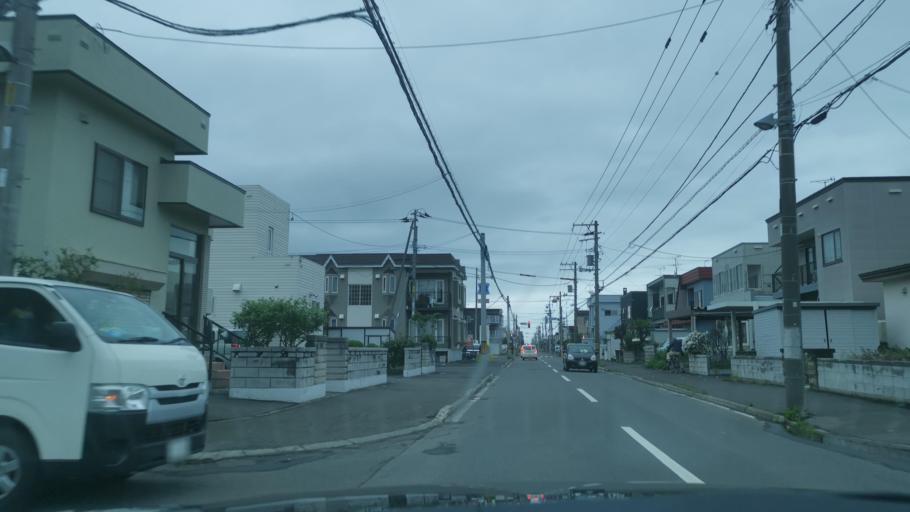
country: JP
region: Hokkaido
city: Sapporo
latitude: 43.1048
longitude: 141.3077
